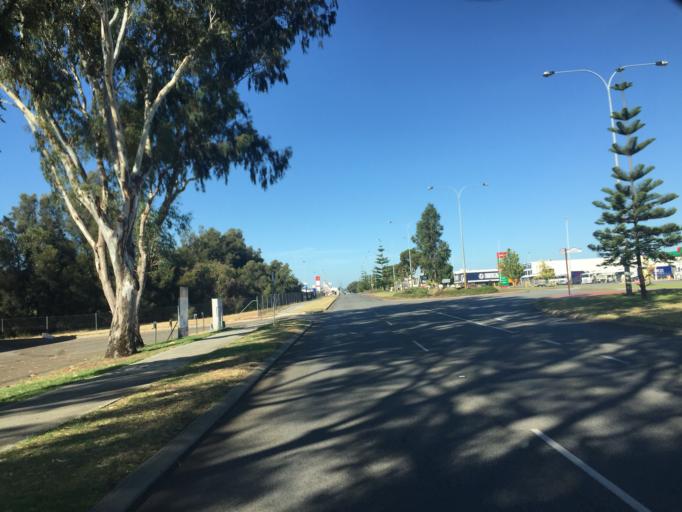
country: AU
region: Western Australia
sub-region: Canning
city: Queens Park
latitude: -31.9917
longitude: 115.9455
